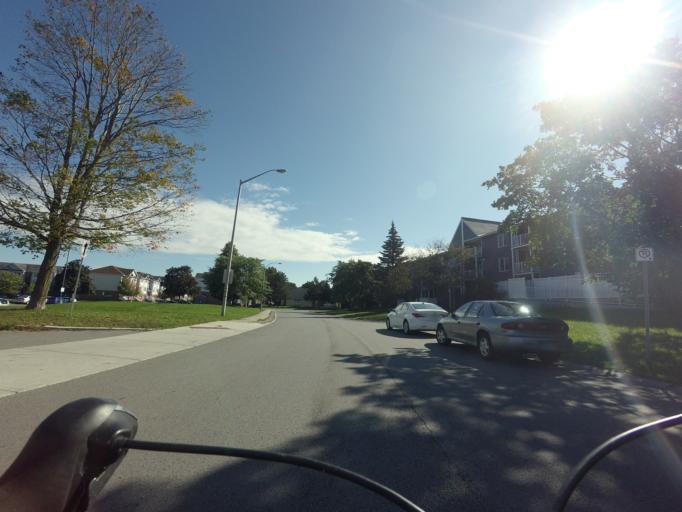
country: CA
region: Ontario
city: Bells Corners
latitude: 45.3136
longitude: -75.8326
